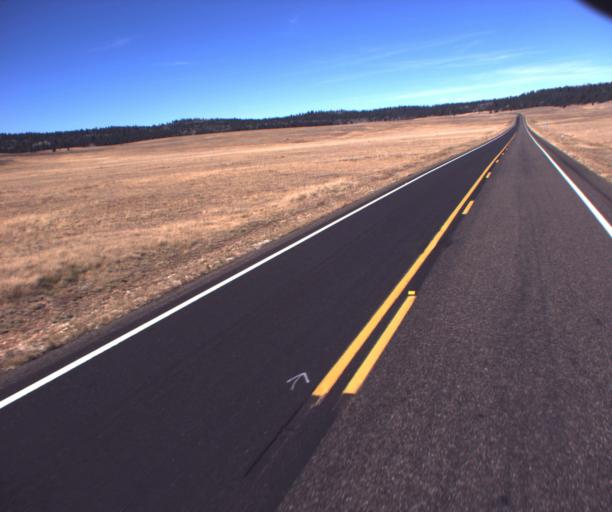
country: US
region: Arizona
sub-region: Coconino County
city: Grand Canyon
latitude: 36.4823
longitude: -112.1277
